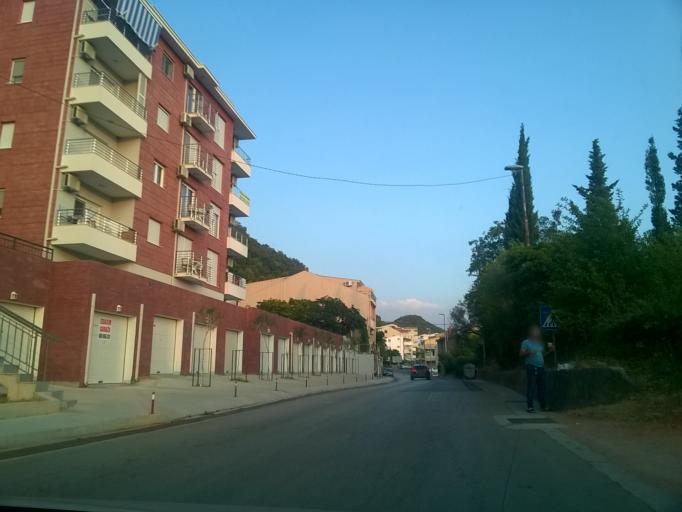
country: ME
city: Petrovac na Moru
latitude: 42.2070
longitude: 18.9464
